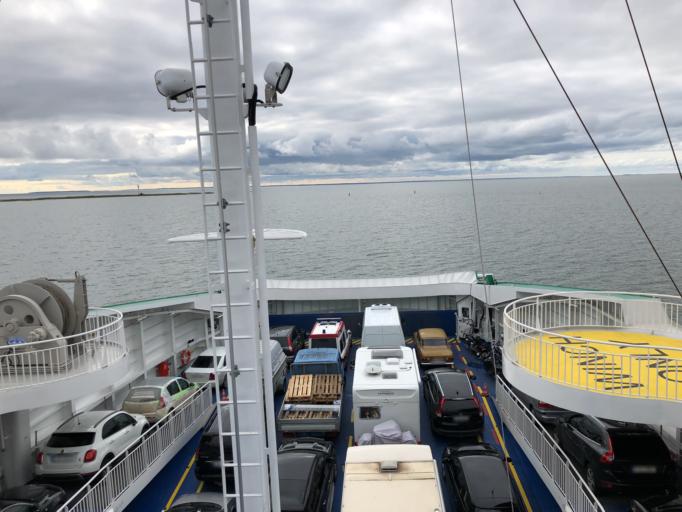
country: EE
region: Laeaene
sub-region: Vormsi vald
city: Hullo
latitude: 58.9078
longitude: 23.3658
